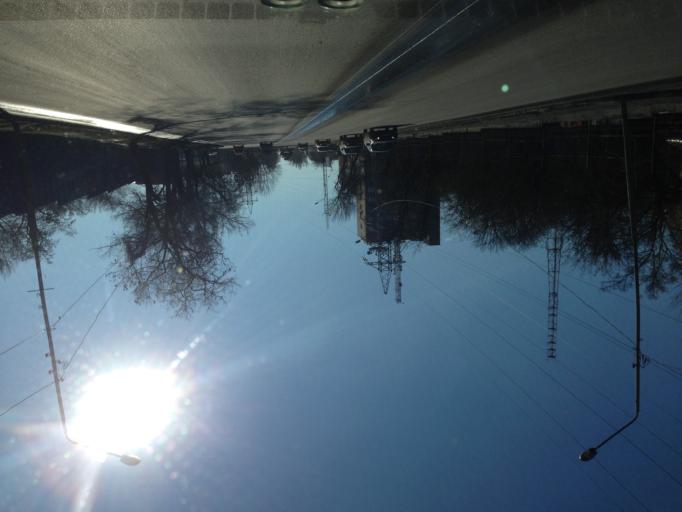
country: RU
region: Rostov
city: Rostov-na-Donu
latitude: 47.2419
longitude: 39.7344
